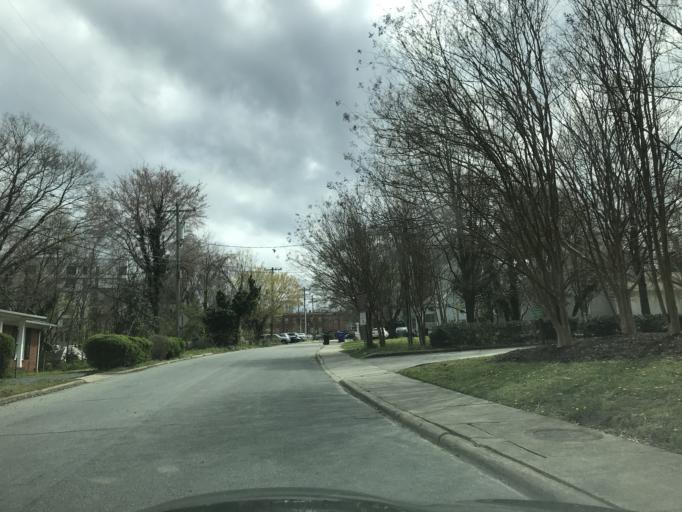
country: US
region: North Carolina
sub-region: Orange County
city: Chapel Hill
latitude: 35.9131
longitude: -79.0626
